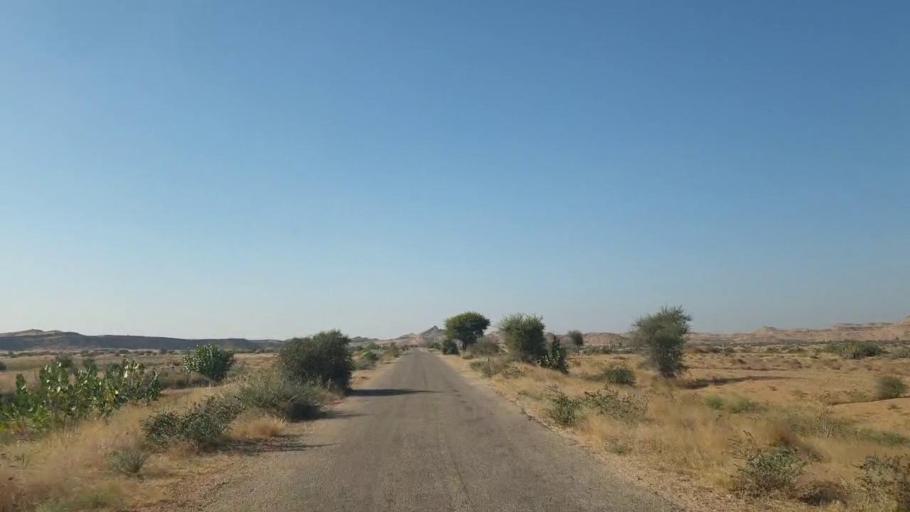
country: PK
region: Sindh
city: Malir Cantonment
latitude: 25.3940
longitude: 67.4977
